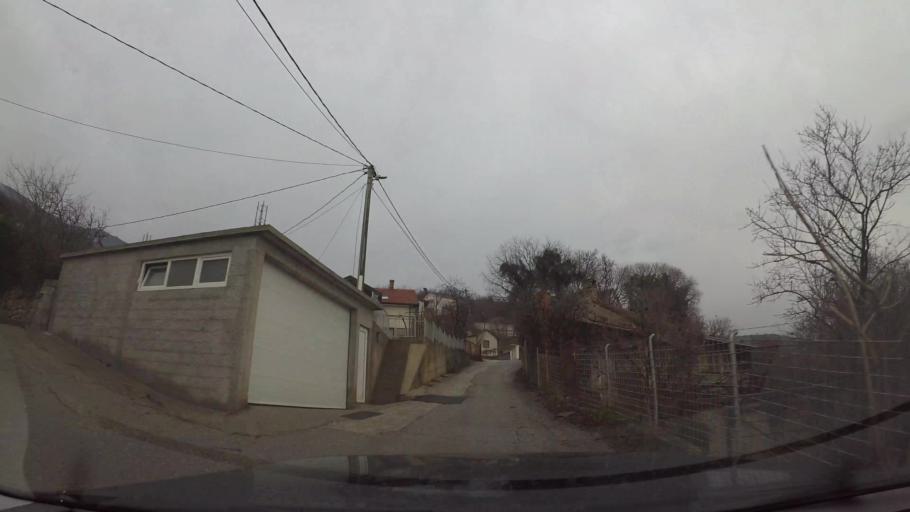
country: BA
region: Federation of Bosnia and Herzegovina
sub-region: Hercegovacko-Bosanski Kanton
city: Mostar
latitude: 43.3629
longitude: 17.8027
